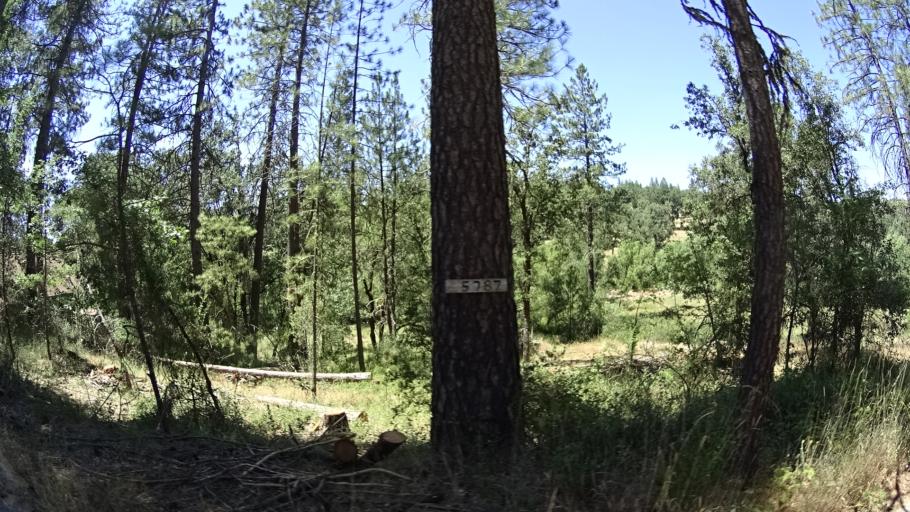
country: US
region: California
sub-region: Calaveras County
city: Mountain Ranch
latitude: 38.2698
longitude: -120.4962
